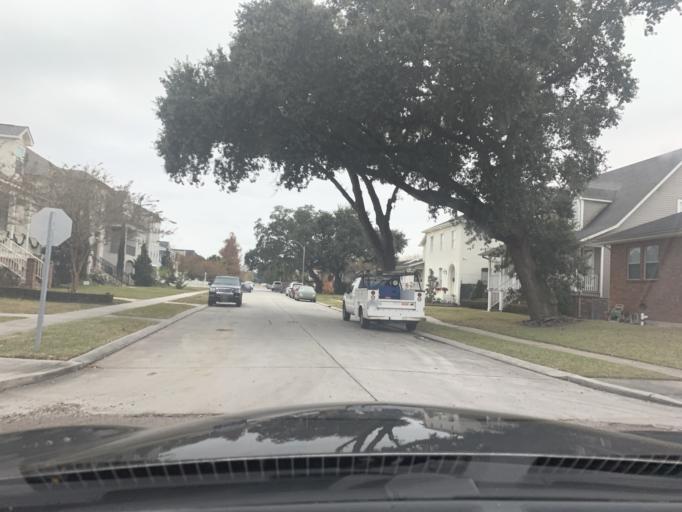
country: US
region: Louisiana
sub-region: Jefferson Parish
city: Metairie
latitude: 30.0108
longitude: -90.1107
